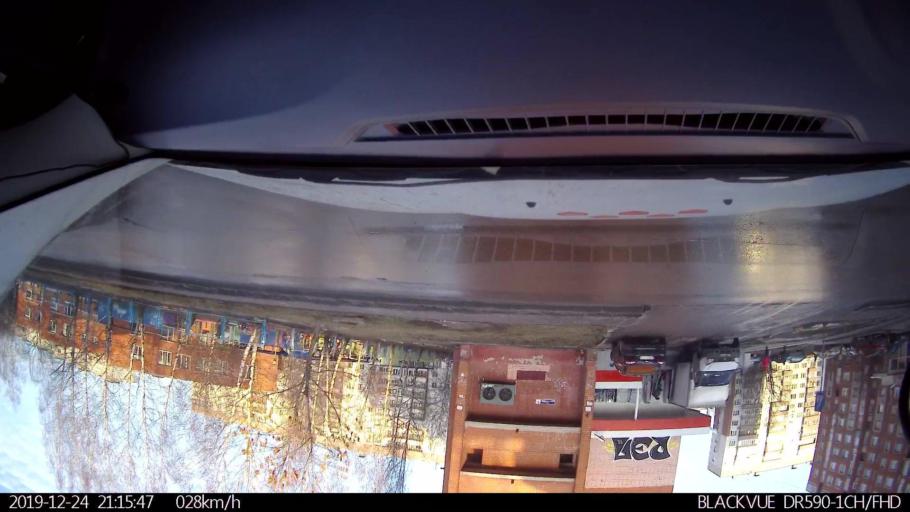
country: RU
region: Nizjnij Novgorod
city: Nizhniy Novgorod
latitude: 56.2671
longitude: 43.8826
